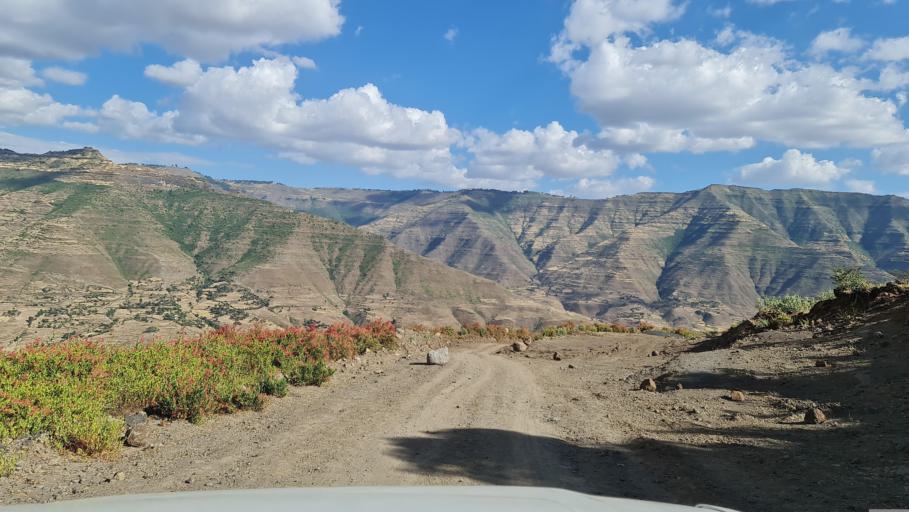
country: ET
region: Amhara
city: Debark'
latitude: 13.1237
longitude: 38.0200
